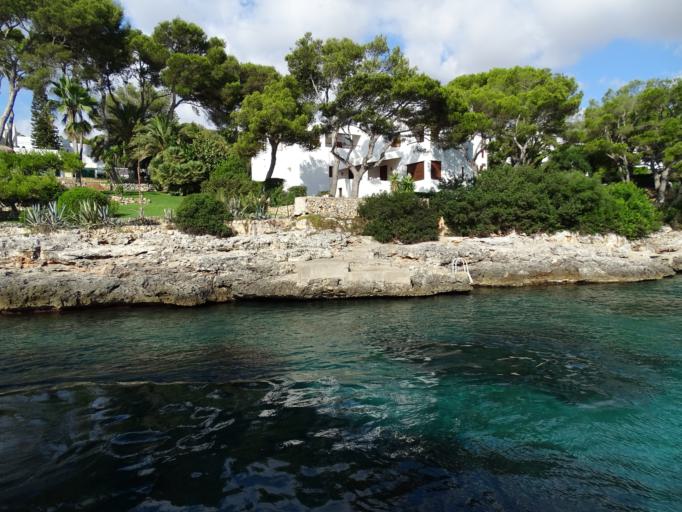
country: ES
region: Balearic Islands
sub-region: Illes Balears
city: Santanyi
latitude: 39.3720
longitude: 3.2332
